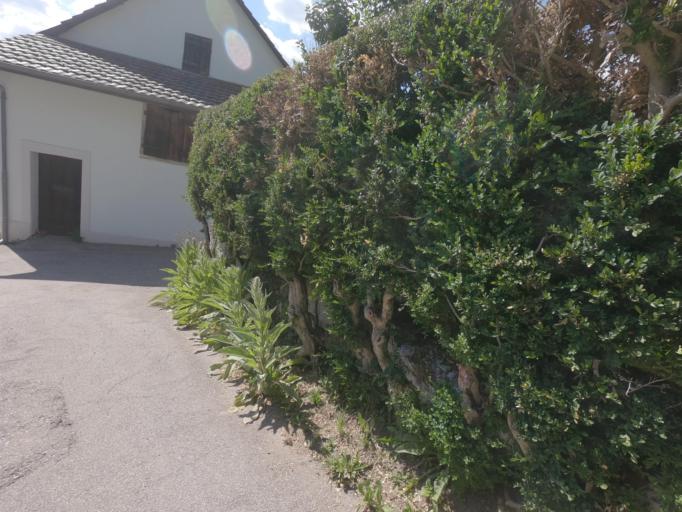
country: CH
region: Solothurn
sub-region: Bezirk Lebern
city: Langendorf
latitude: 47.2306
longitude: 7.5332
